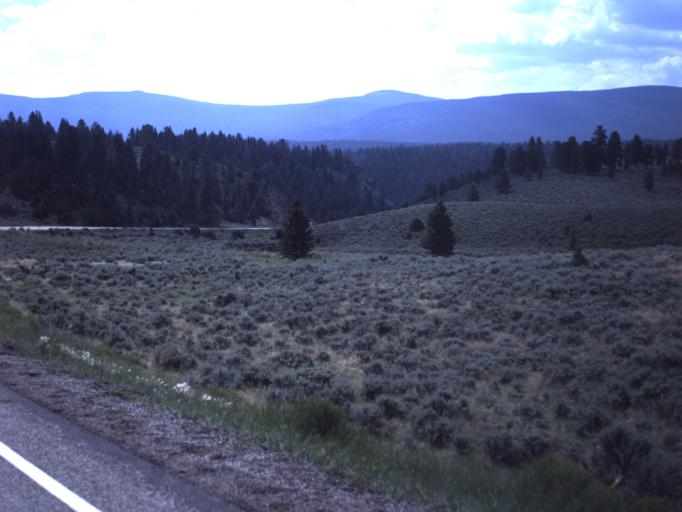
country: US
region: Utah
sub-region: Daggett County
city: Manila
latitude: 40.8826
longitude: -109.6938
